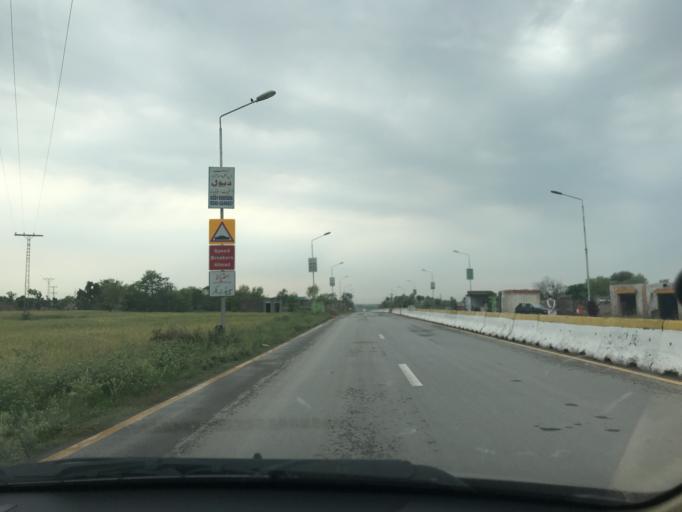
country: PK
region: Islamabad
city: Islamabad
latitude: 33.7017
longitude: 73.1882
